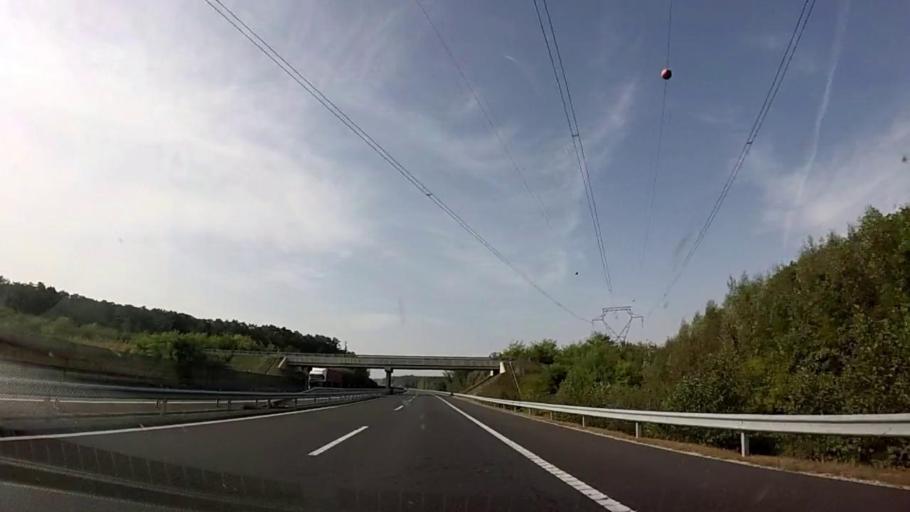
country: HU
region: Zala
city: Zalakomar
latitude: 46.5037
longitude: 17.1452
